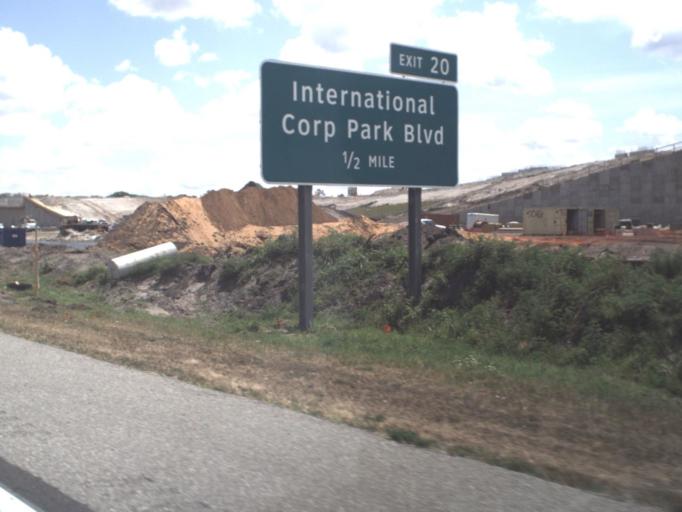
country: US
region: Florida
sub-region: Orange County
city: Wedgefield
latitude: 28.4516
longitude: -81.1737
